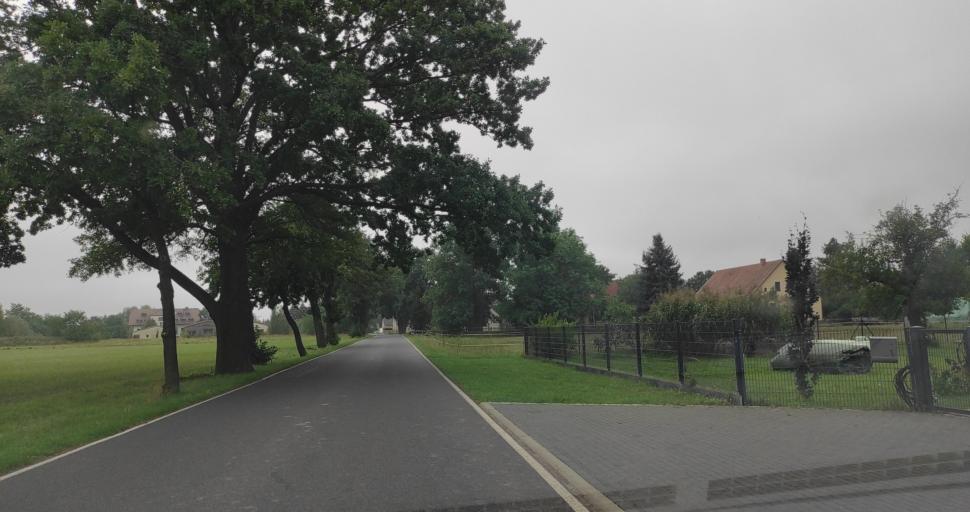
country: DE
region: Brandenburg
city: Forst
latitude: 51.6950
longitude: 14.6295
